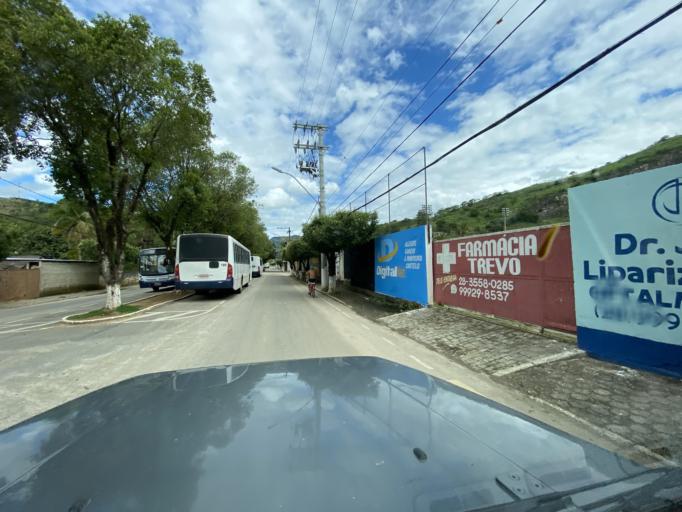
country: BR
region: Espirito Santo
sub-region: Jeronimo Monteiro
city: Jeronimo Monteiro
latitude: -20.7888
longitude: -41.3902
